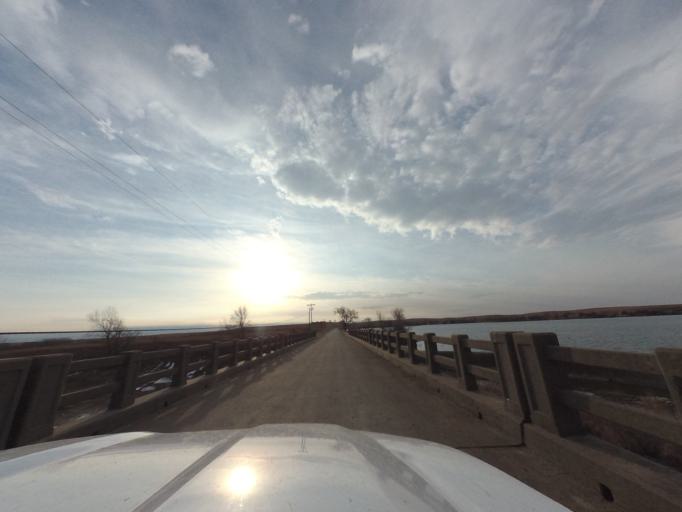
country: US
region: Kansas
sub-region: Morris County
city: Council Grove
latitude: 38.5288
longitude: -96.4158
